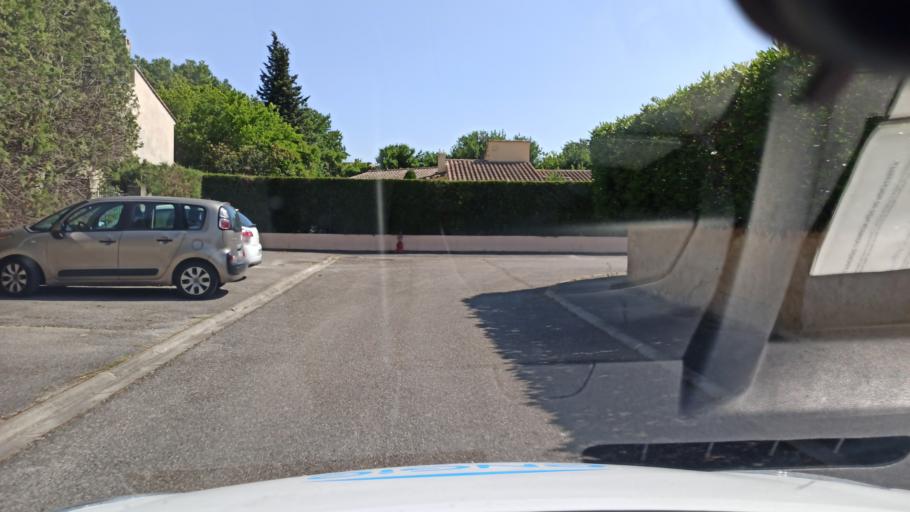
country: FR
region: Provence-Alpes-Cote d'Azur
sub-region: Departement du Vaucluse
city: Morieres-les-Avignon
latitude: 43.9564
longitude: 4.8860
